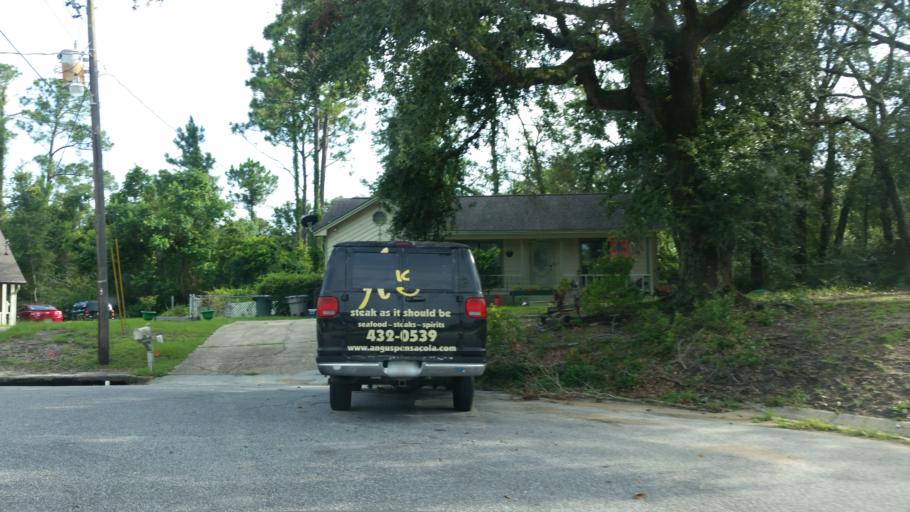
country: US
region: Florida
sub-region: Escambia County
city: Ferry Pass
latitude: 30.5108
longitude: -87.1732
